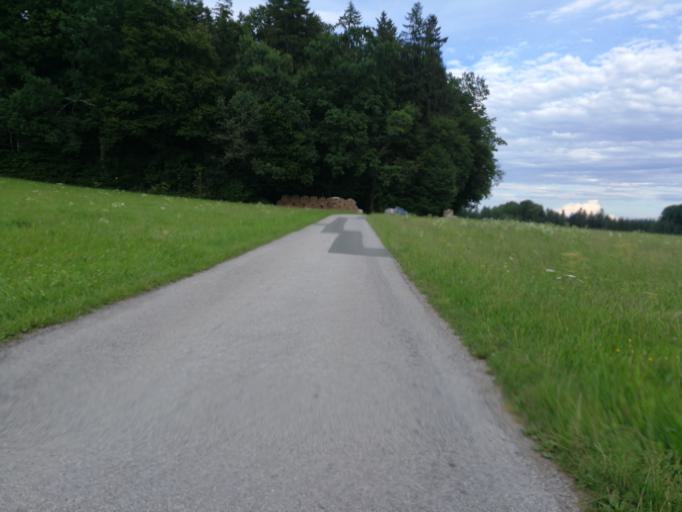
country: AT
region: Salzburg
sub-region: Politischer Bezirk Salzburg-Umgebung
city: Anthering
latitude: 47.8796
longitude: 13.0380
